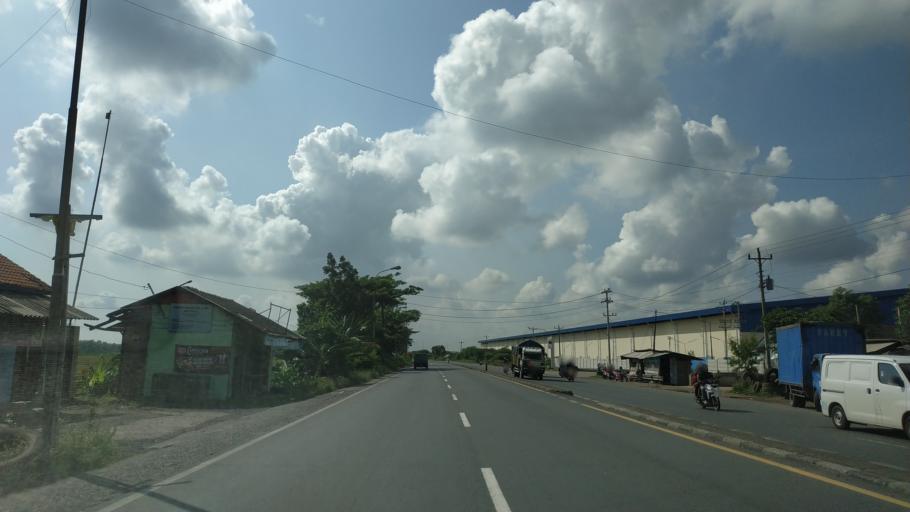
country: ID
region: Central Java
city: Wiradesa
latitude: -6.8876
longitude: 109.5754
